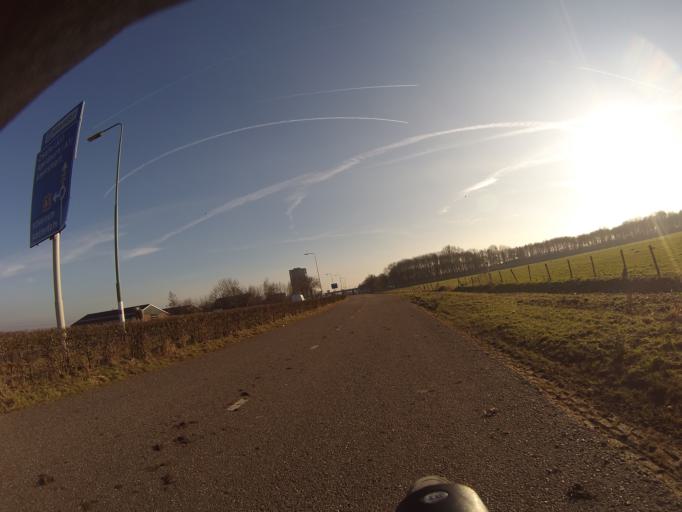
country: NL
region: Utrecht
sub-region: Gemeente Amersfoort
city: Hoogland
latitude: 52.2118
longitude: 5.3644
